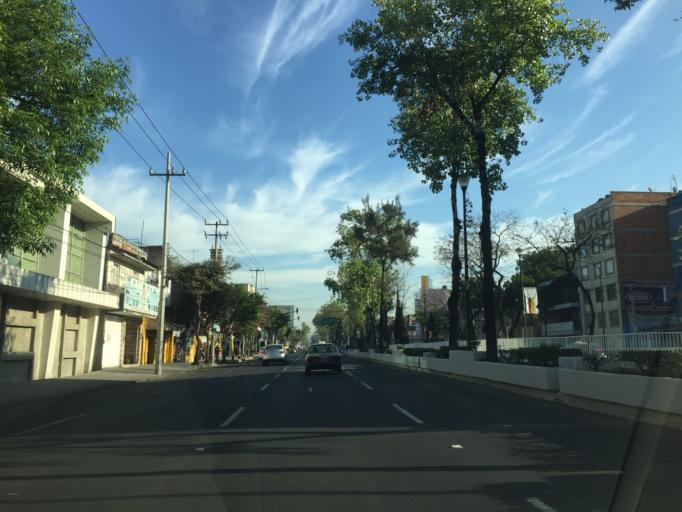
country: MX
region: Mexico City
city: Cuauhtemoc
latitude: 19.4583
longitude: -99.1276
